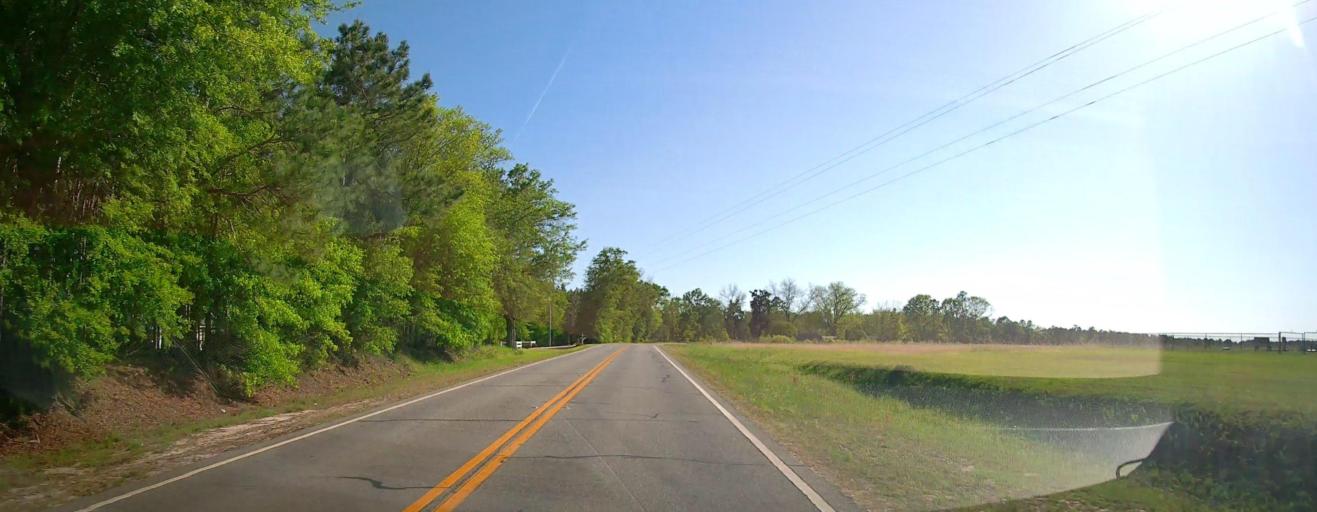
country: US
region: Georgia
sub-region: Wilcox County
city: Rochelle
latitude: 31.9067
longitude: -83.4821
